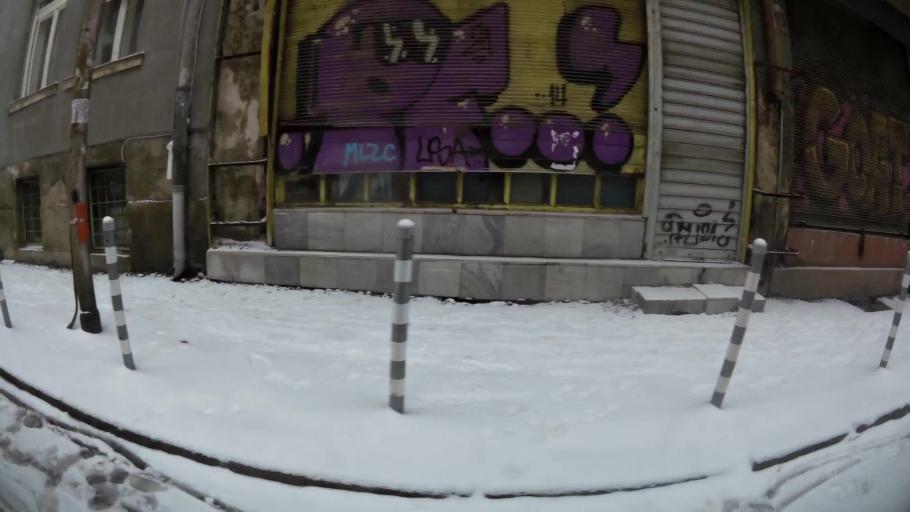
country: BG
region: Sofia-Capital
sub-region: Stolichna Obshtina
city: Sofia
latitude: 42.7029
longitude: 23.3184
